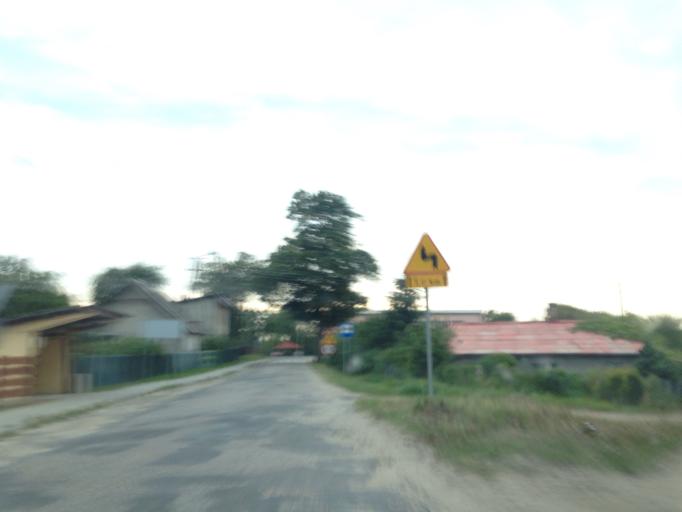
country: PL
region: Kujawsko-Pomorskie
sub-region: Powiat brodnicki
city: Brzozie
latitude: 53.2892
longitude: 19.6912
